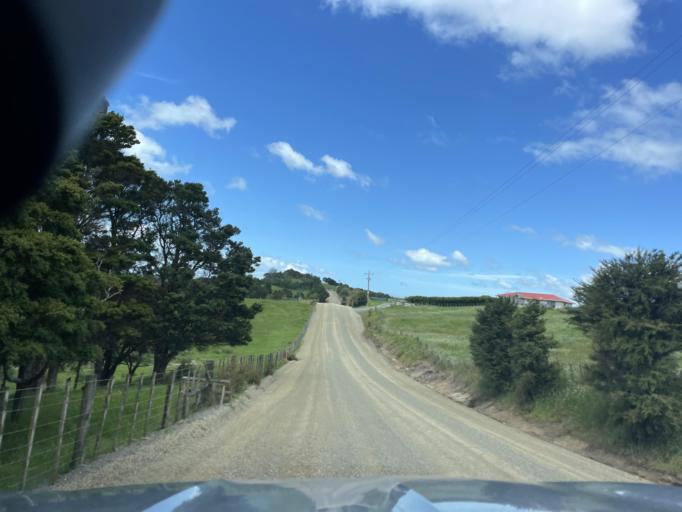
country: NZ
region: Auckland
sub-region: Auckland
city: Wellsford
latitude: -36.1572
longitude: 174.2868
